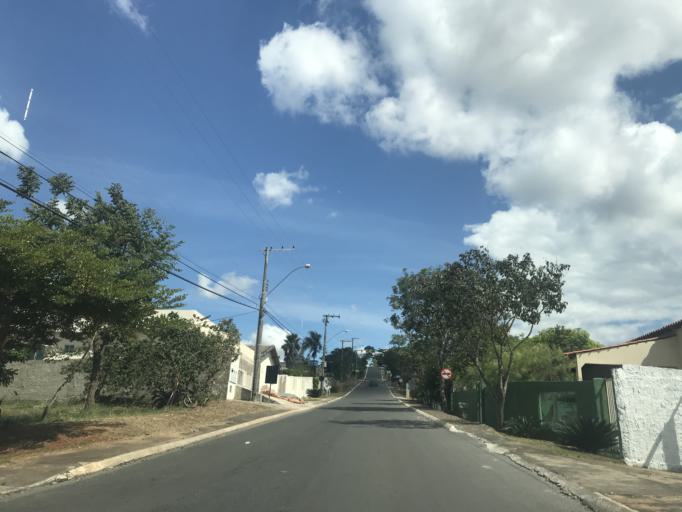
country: BR
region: Federal District
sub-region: Brasilia
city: Brasilia
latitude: -15.8671
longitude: -47.7542
